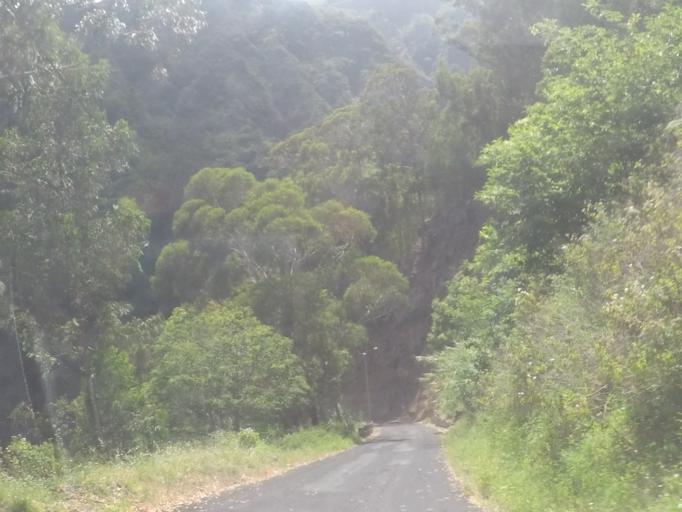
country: PT
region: Madeira
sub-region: Camara de Lobos
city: Curral das Freiras
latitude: 32.7166
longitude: -16.9751
